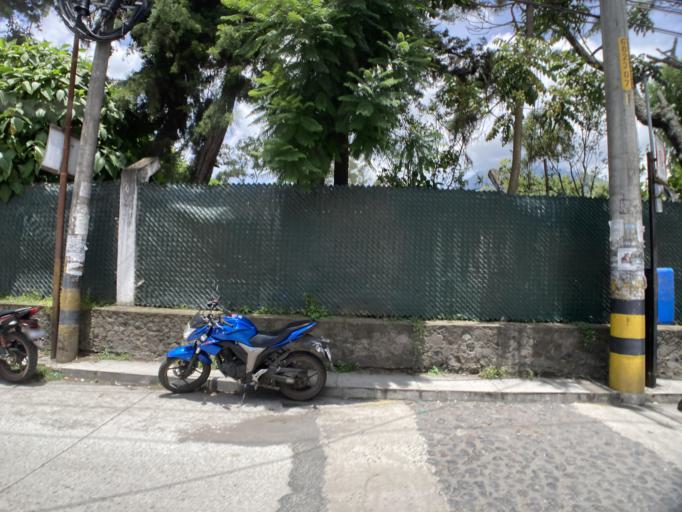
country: GT
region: Sacatepequez
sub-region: Municipio de Santa Maria de Jesus
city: Santa Maria de Jesus
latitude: 14.5340
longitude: -90.7332
